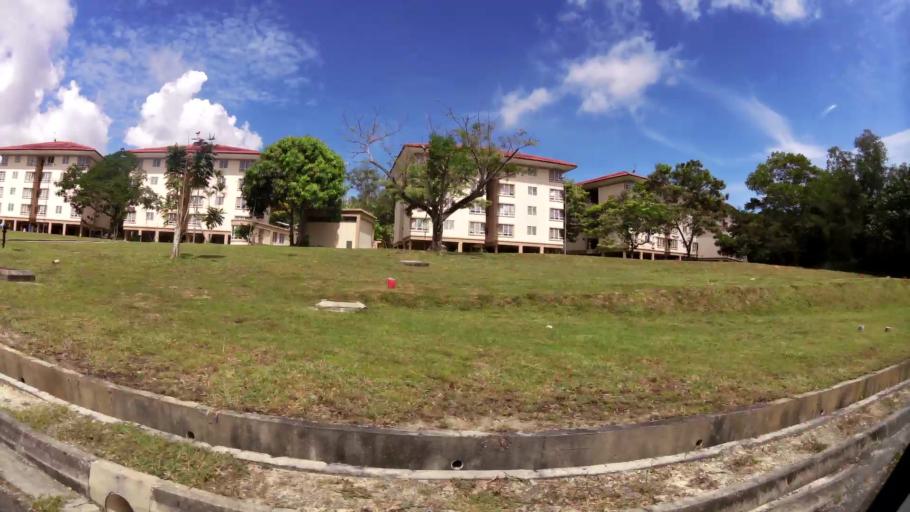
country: BN
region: Brunei and Muara
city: Bandar Seri Begawan
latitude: 4.9354
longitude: 114.8898
